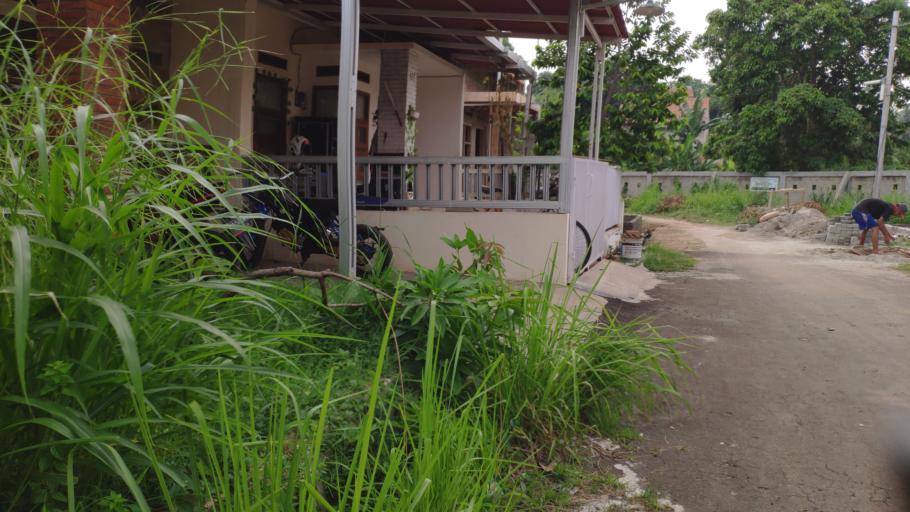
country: ID
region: West Java
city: Depok
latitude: -6.3785
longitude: 106.7972
